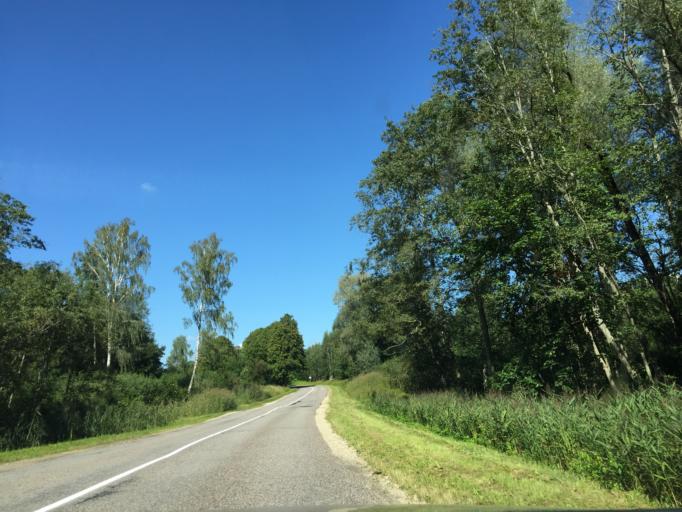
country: LV
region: Limbazu Rajons
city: Limbazi
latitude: 57.4754
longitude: 24.7107
